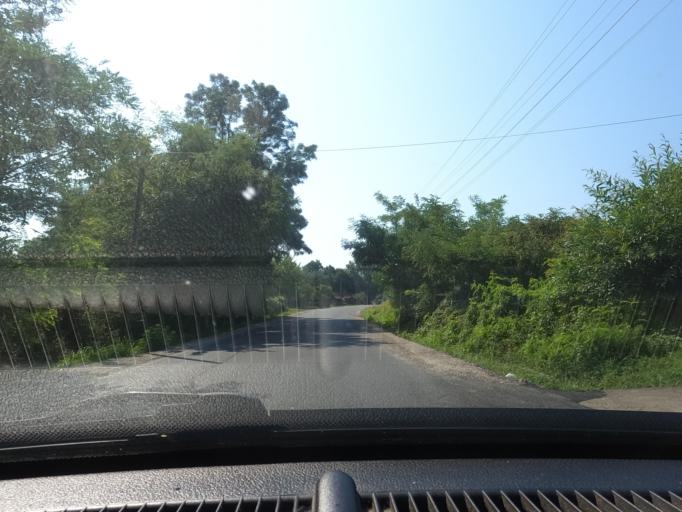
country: RS
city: Kozjak
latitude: 44.5646
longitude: 19.2895
